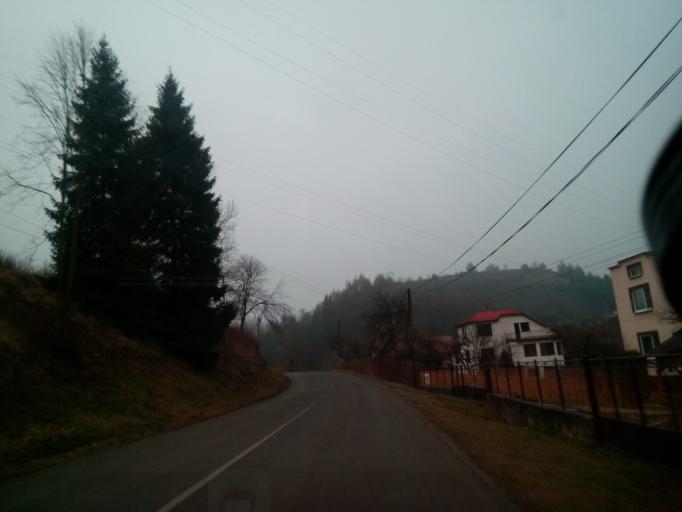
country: SK
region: Kosicky
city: Krompachy
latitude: 48.9539
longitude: 20.9536
